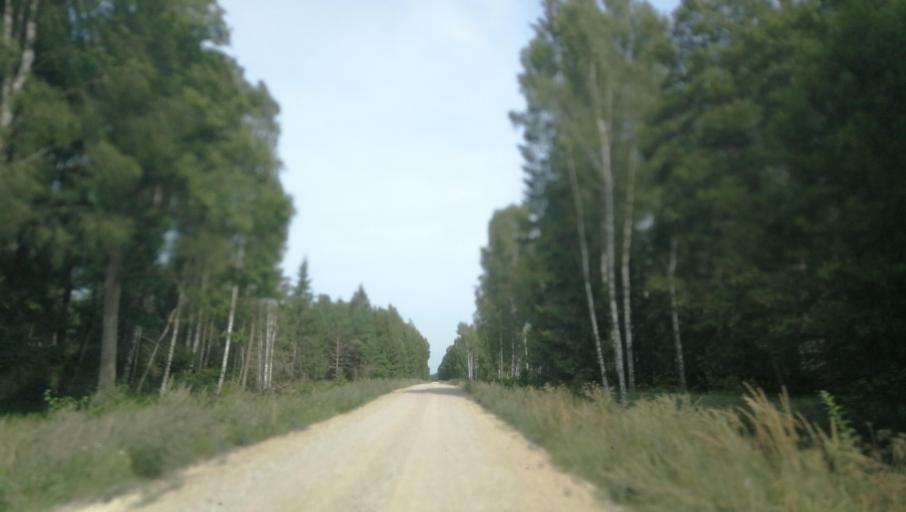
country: LV
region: Durbe
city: Liegi
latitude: 56.7790
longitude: 21.3518
